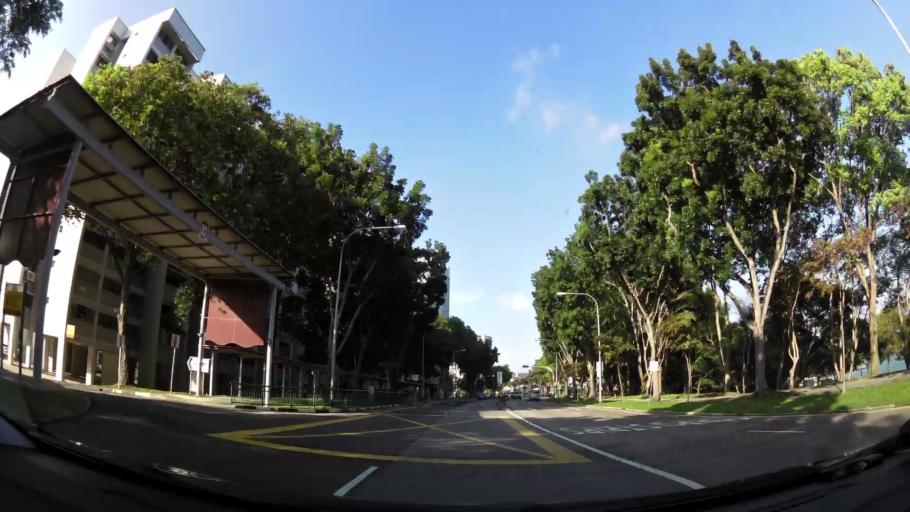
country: SG
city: Singapore
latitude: 1.3384
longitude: 103.9259
